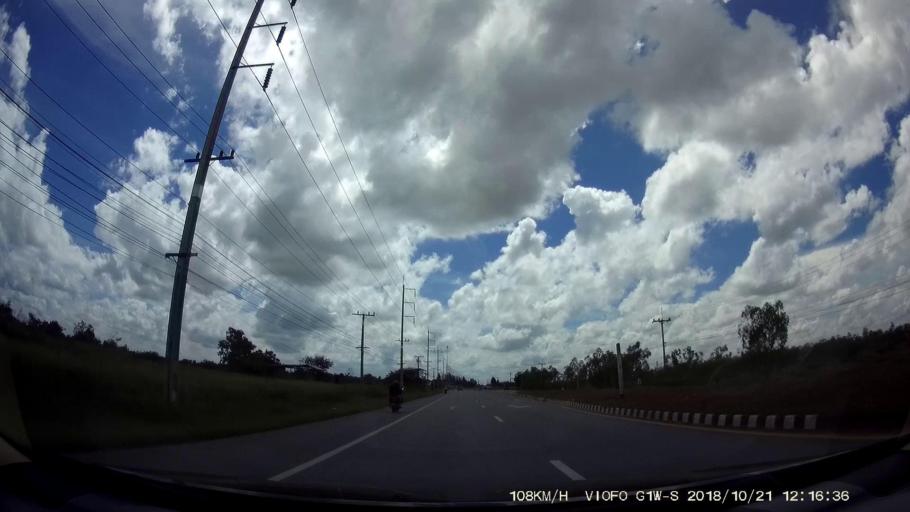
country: TH
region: Nakhon Ratchasima
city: Dan Khun Thot
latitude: 15.3448
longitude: 101.8250
